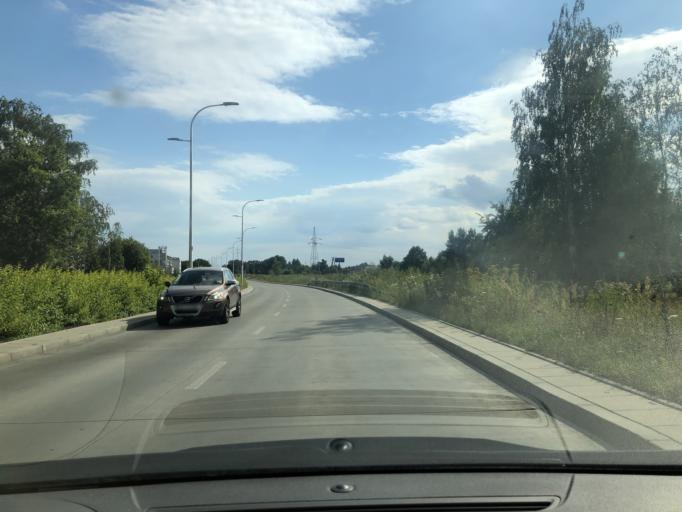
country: PL
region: Lower Silesian Voivodeship
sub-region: Powiat wroclawski
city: Smolec
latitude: 51.1489
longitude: 16.9092
